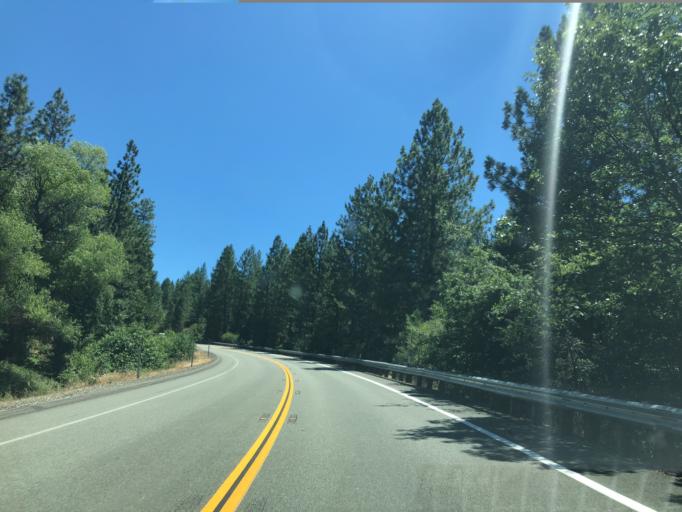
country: US
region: California
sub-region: Shasta County
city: Shingletown
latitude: 40.5015
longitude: -121.9295
